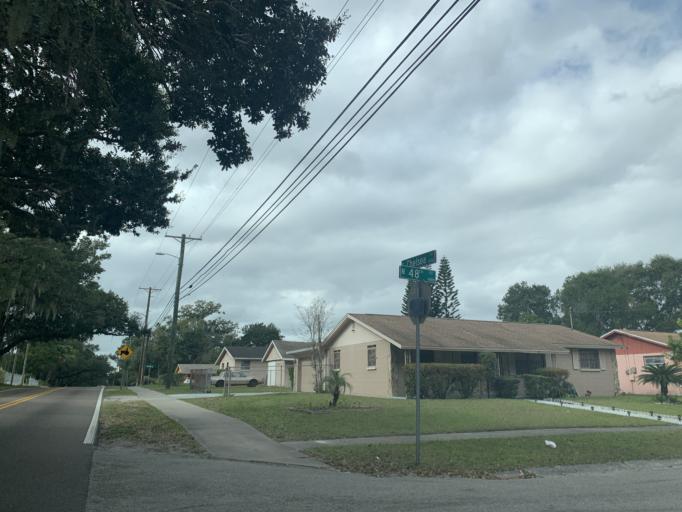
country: US
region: Florida
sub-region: Hillsborough County
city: East Lake-Orient Park
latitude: 27.9852
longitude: -82.4037
